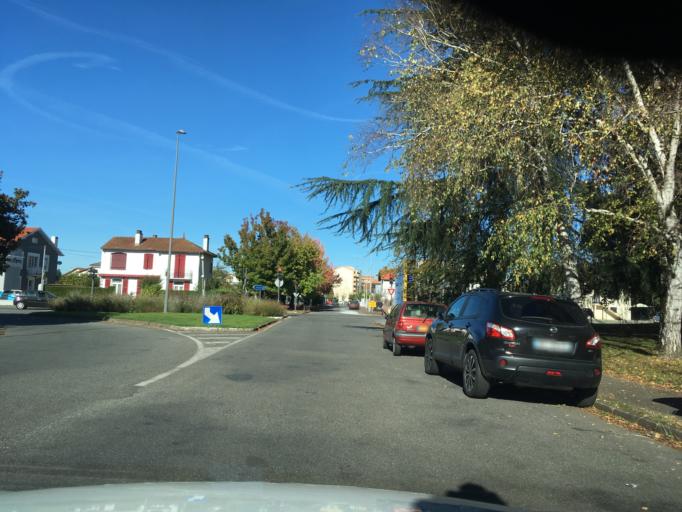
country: FR
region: Aquitaine
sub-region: Departement des Pyrenees-Atlantiques
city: Pau
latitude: 43.3107
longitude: -0.3598
